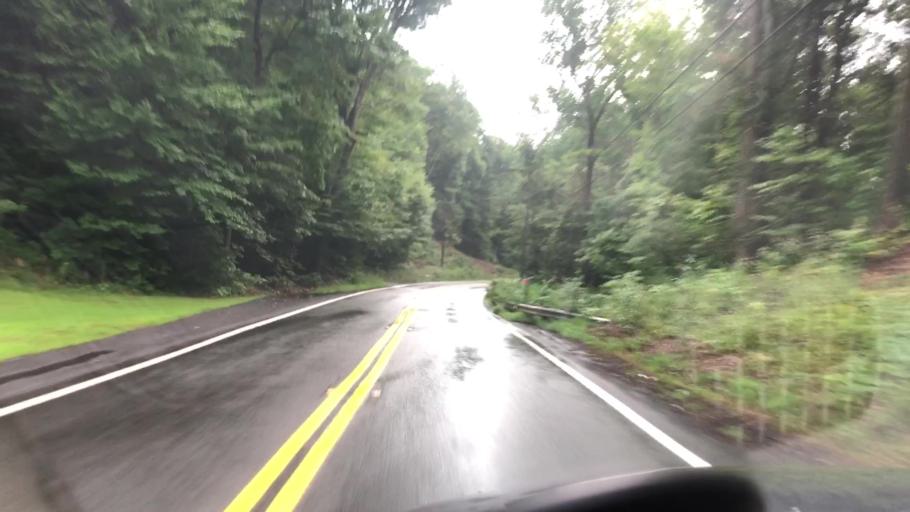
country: US
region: Massachusetts
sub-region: Hampshire County
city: Westhampton
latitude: 42.2658
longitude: -72.8661
